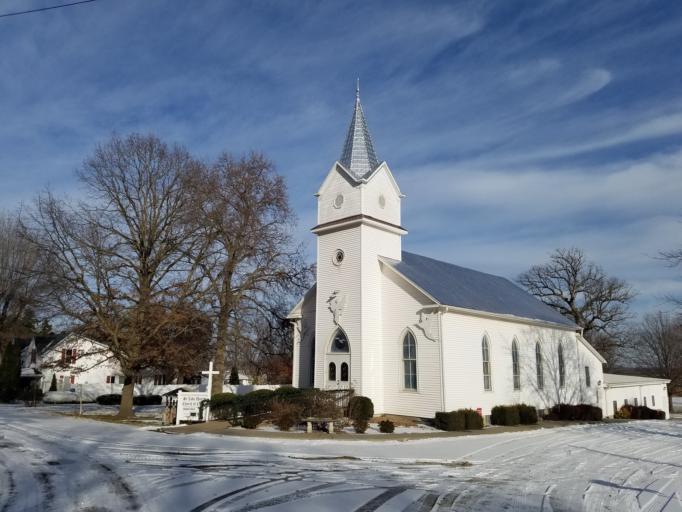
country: US
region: Missouri
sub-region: Carroll County
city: Carrollton
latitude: 39.2048
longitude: -93.4414
